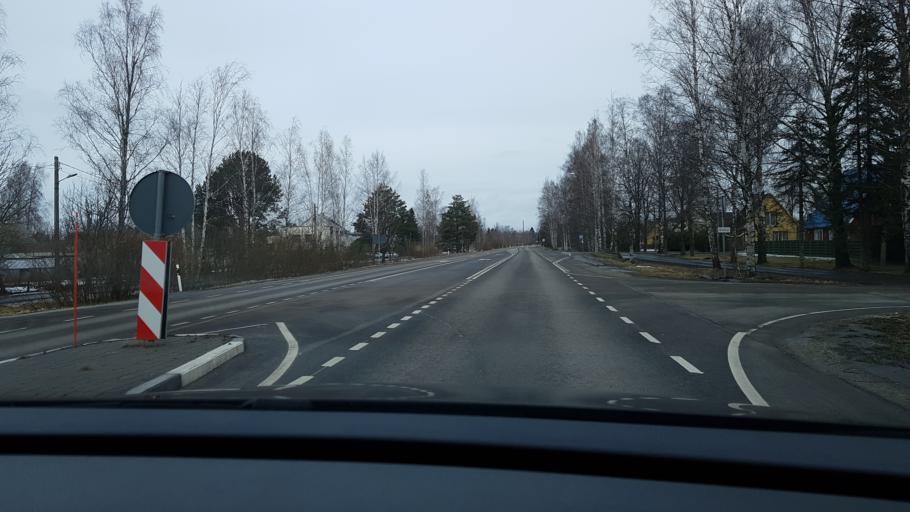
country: EE
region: Paernumaa
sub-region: Paikuse vald
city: Paikuse
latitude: 58.3961
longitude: 24.6468
